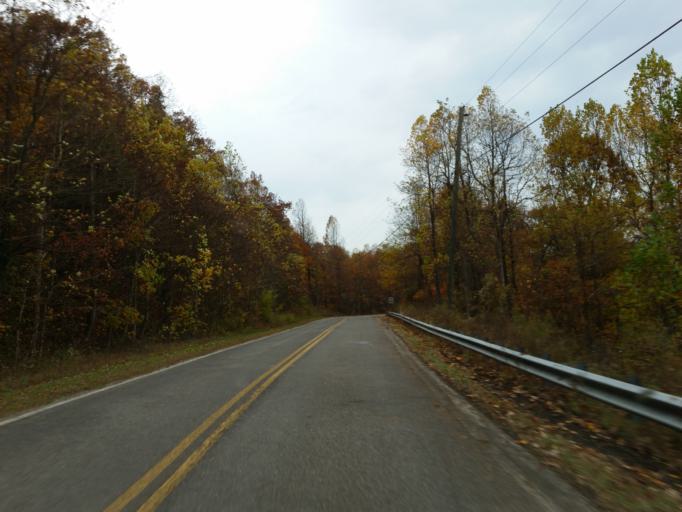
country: US
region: Georgia
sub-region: Pickens County
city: Jasper
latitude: 34.5493
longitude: -84.3509
